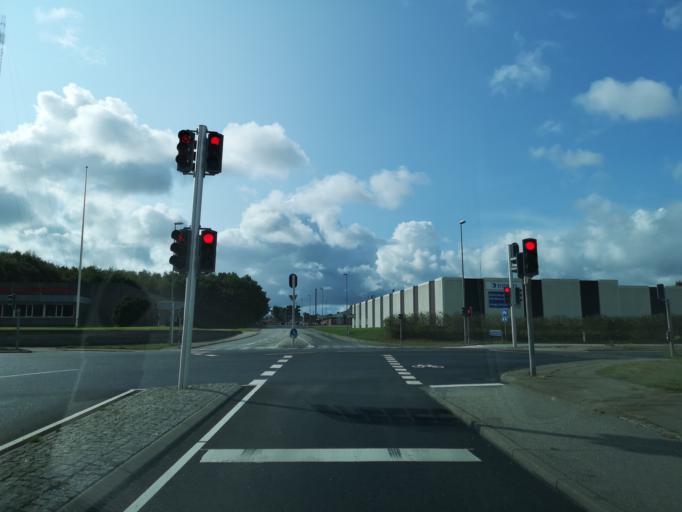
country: DK
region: Central Jutland
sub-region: Herning Kommune
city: Herning
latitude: 56.1340
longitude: 8.9391
